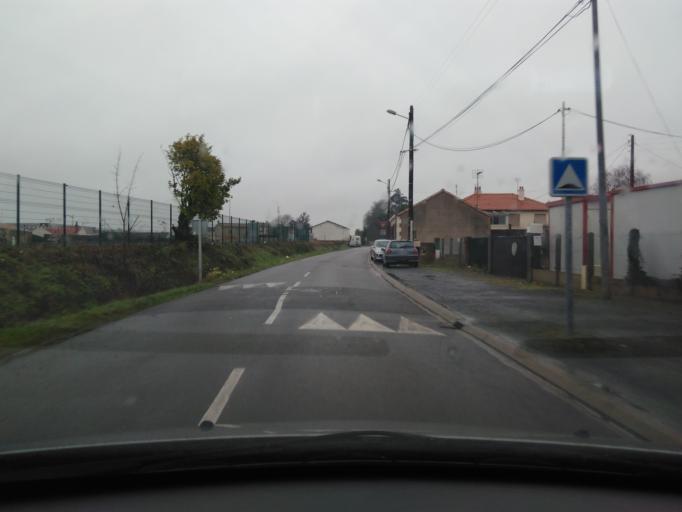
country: FR
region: Pays de la Loire
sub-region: Departement de la Vendee
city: Lucon
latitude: 46.4644
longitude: -1.1695
